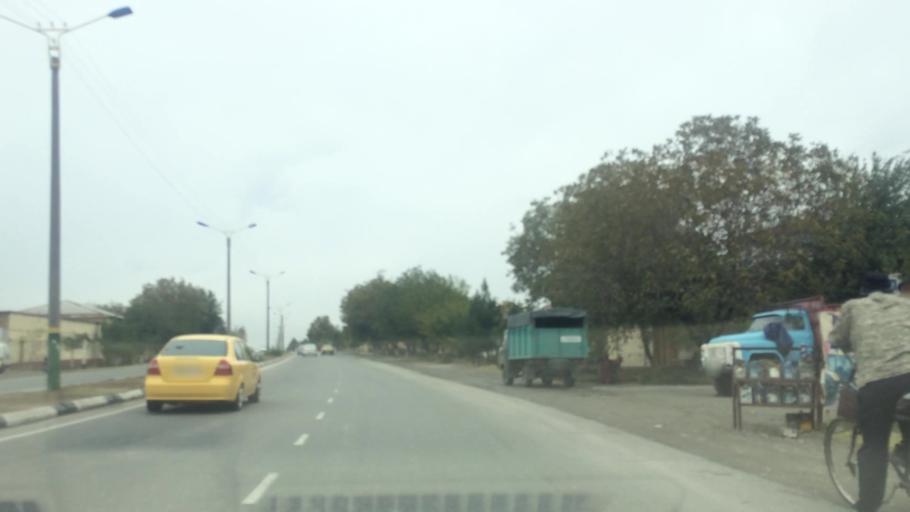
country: UZ
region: Samarqand
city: Bulung'ur
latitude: 39.7684
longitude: 67.2624
